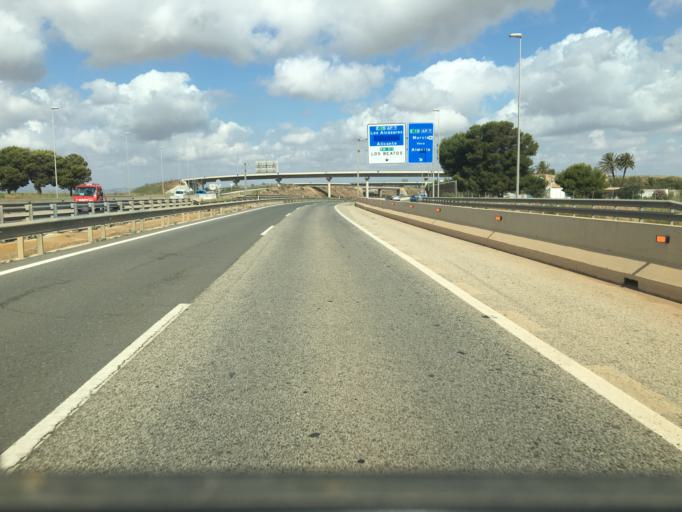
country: ES
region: Murcia
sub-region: Murcia
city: La Union
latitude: 37.6562
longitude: -0.8946
